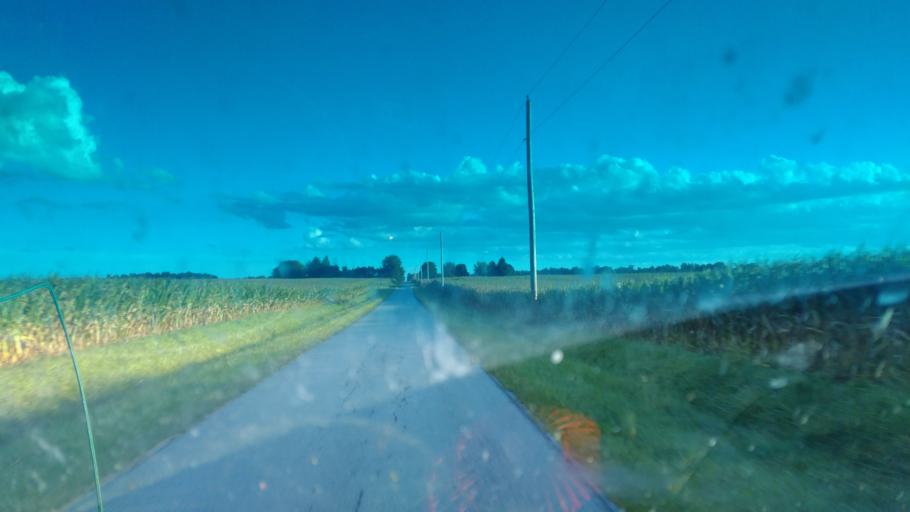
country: US
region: Ohio
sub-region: Wyandot County
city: Upper Sandusky
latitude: 40.8679
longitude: -83.1508
